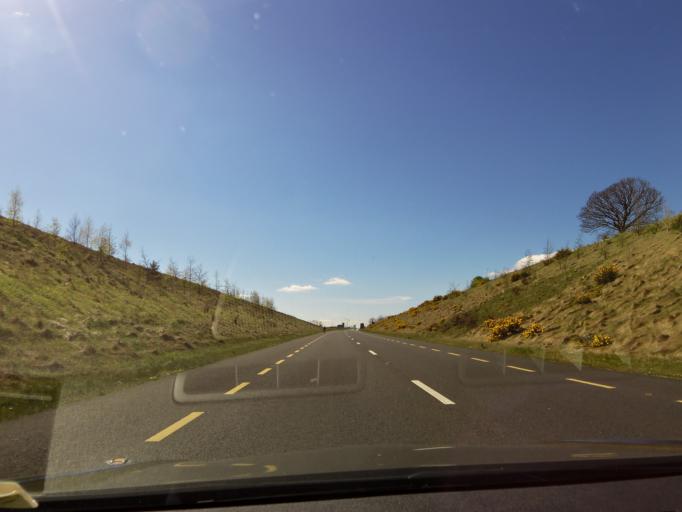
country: IE
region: Leinster
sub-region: Kildare
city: Moone
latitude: 52.9992
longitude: -6.8316
